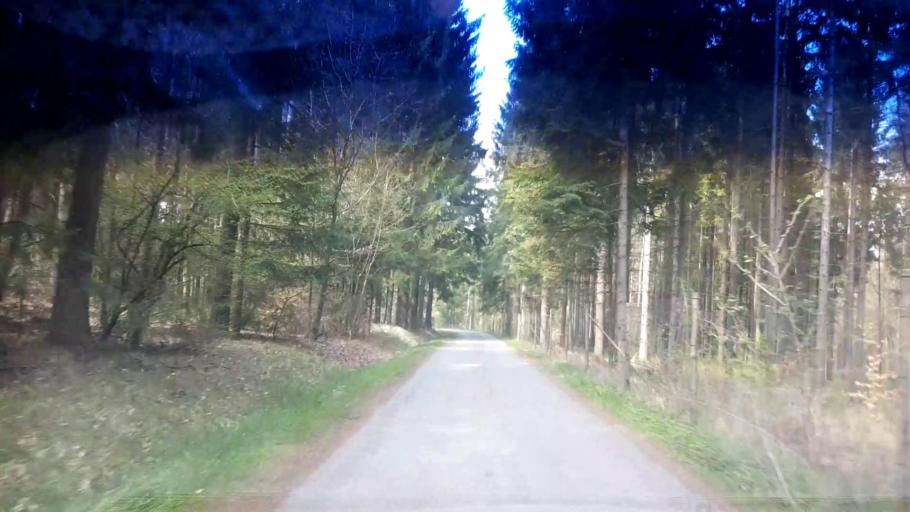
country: DE
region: Bavaria
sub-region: Upper Franconia
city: Poxdorf
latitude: 49.8825
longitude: 11.0879
